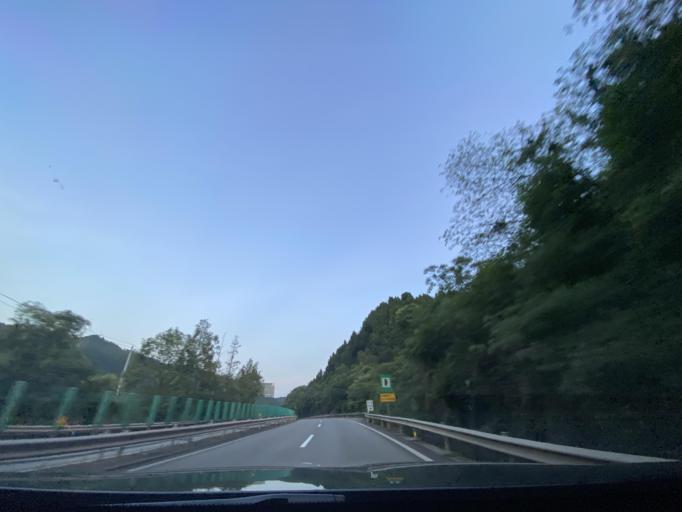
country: CN
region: Sichuan
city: Longquan
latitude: 30.5558
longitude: 104.3499
